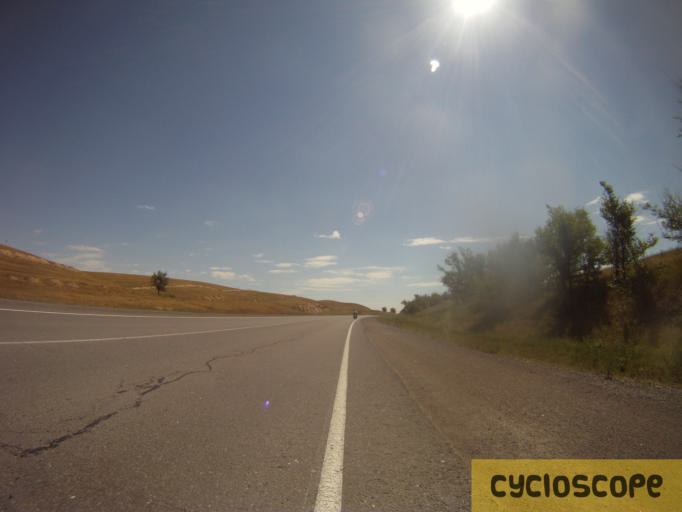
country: KG
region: Chuy
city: Bystrovka
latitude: 43.3358
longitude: 75.8740
